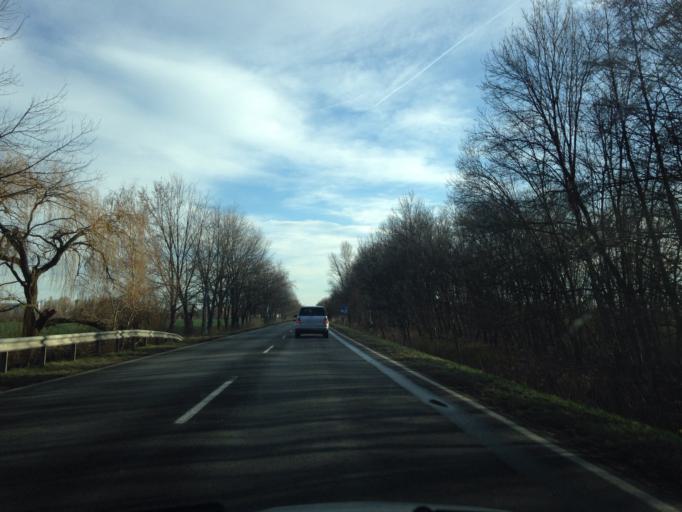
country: HU
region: Gyor-Moson-Sopron
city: Abda
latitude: 47.7086
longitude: 17.5224
